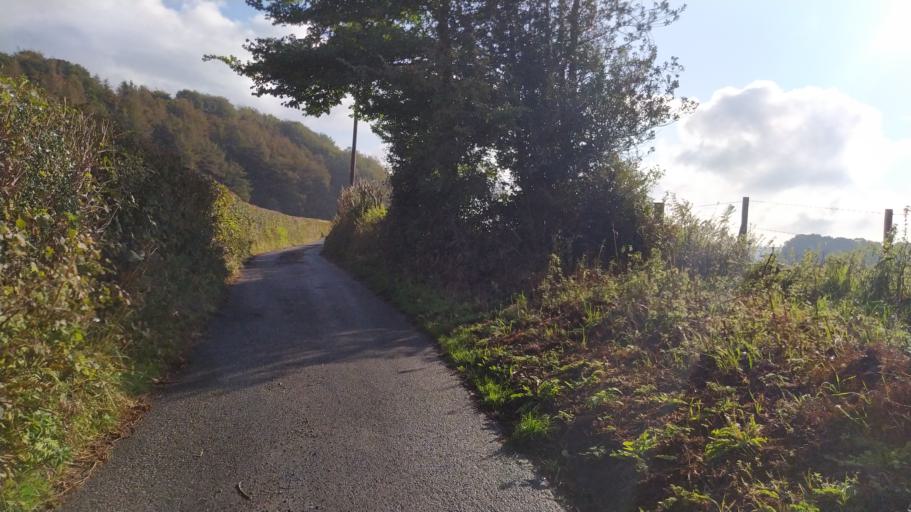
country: GB
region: England
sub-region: Dorset
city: Shaftesbury
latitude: 51.0285
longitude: -2.1388
